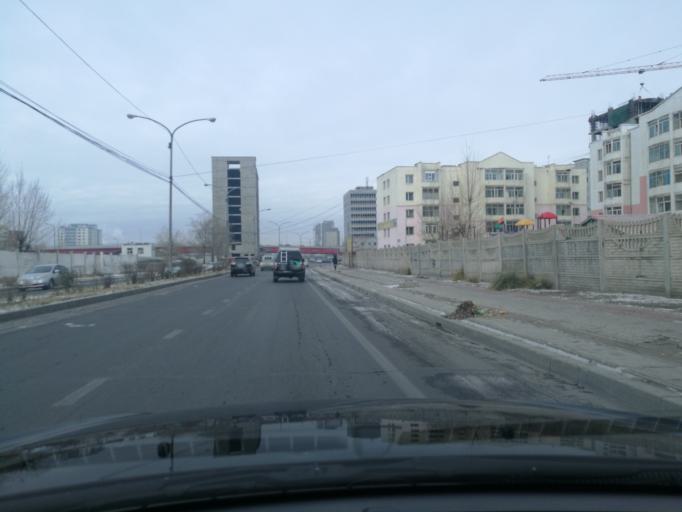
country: MN
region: Ulaanbaatar
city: Ulaanbaatar
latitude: 47.9088
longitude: 106.8994
